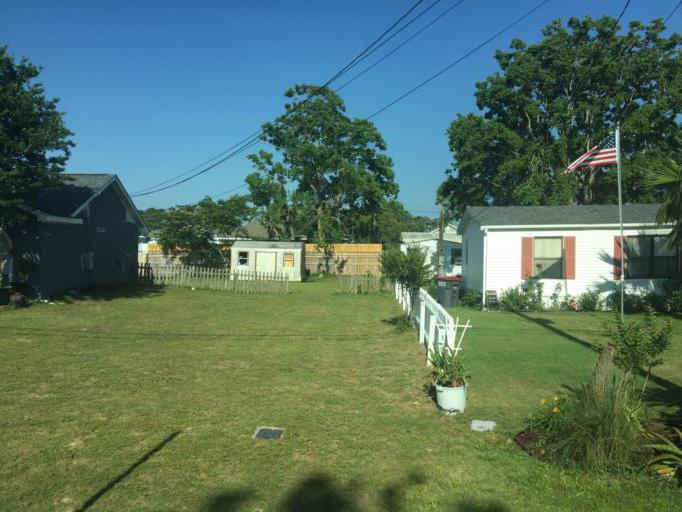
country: US
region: Florida
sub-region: Bay County
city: Panama City Beach
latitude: 30.2024
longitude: -85.8418
